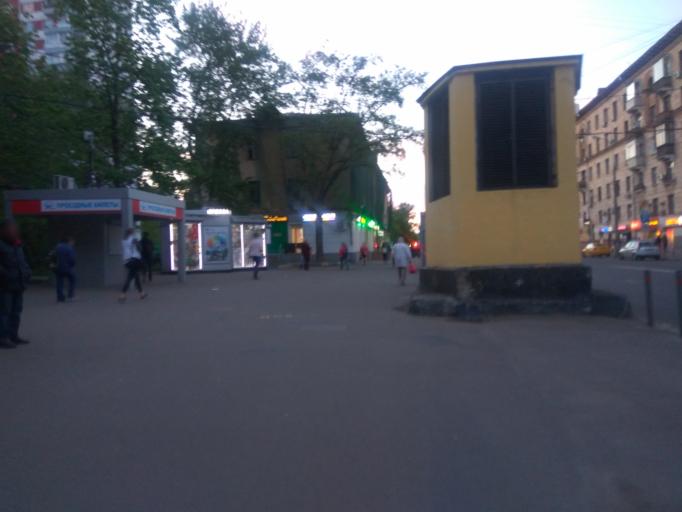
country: RU
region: Moskovskaya
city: Izmaylovo
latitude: 55.7957
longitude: 37.7992
